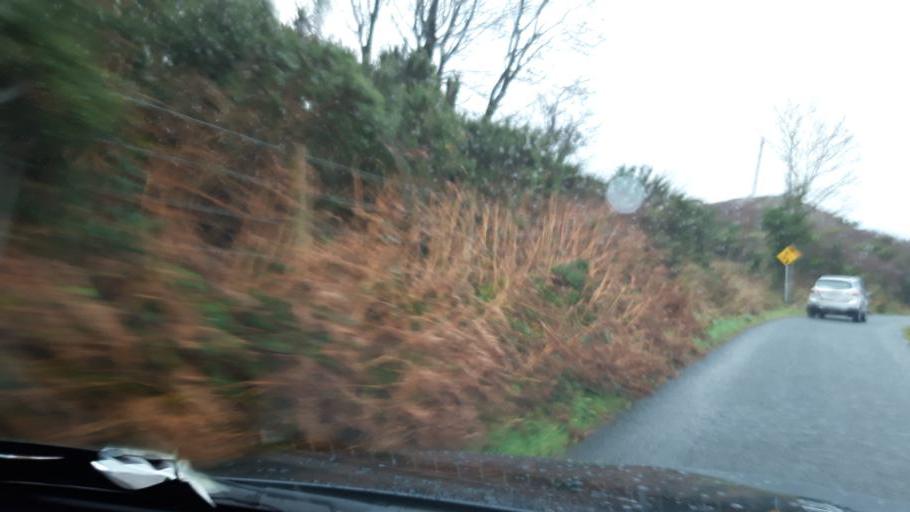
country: IE
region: Ulster
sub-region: County Donegal
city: Ramelton
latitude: 55.2149
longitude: -7.6137
